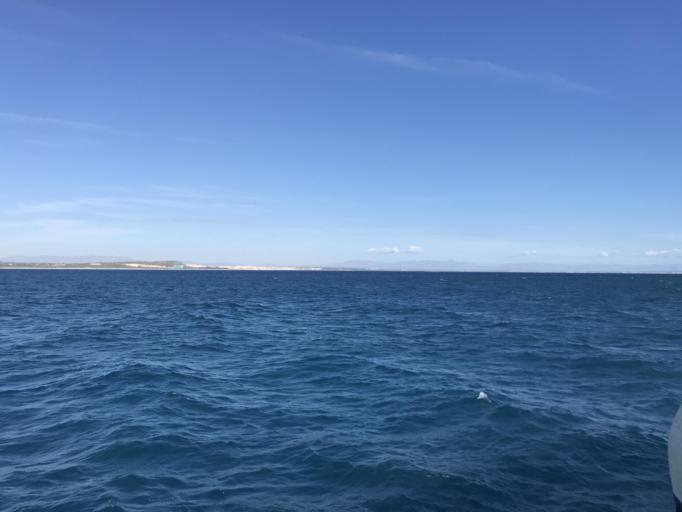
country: ES
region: Valencia
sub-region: Provincia de Alicante
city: Torrevieja
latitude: 38.0210
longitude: -0.6211
